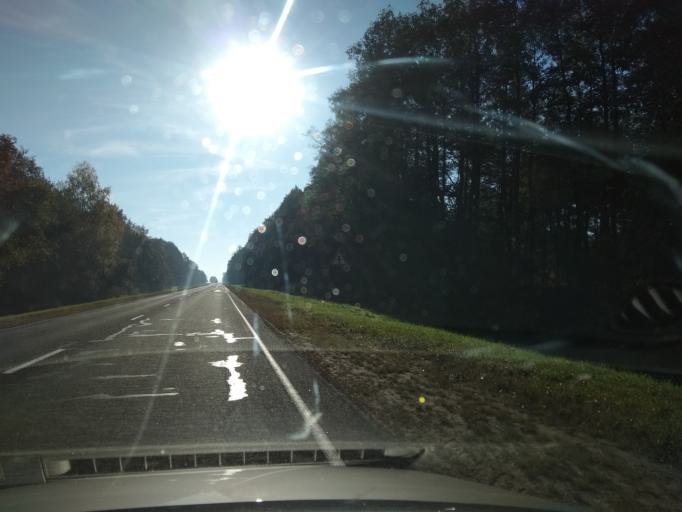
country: BY
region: Brest
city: Malaryta
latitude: 51.8768
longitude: 24.1703
